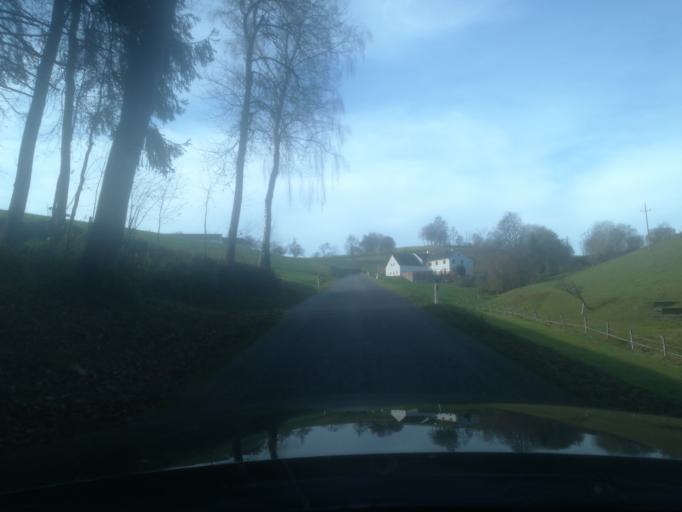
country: AT
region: Upper Austria
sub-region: Politischer Bezirk Perg
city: Perg
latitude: 48.3234
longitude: 14.6584
